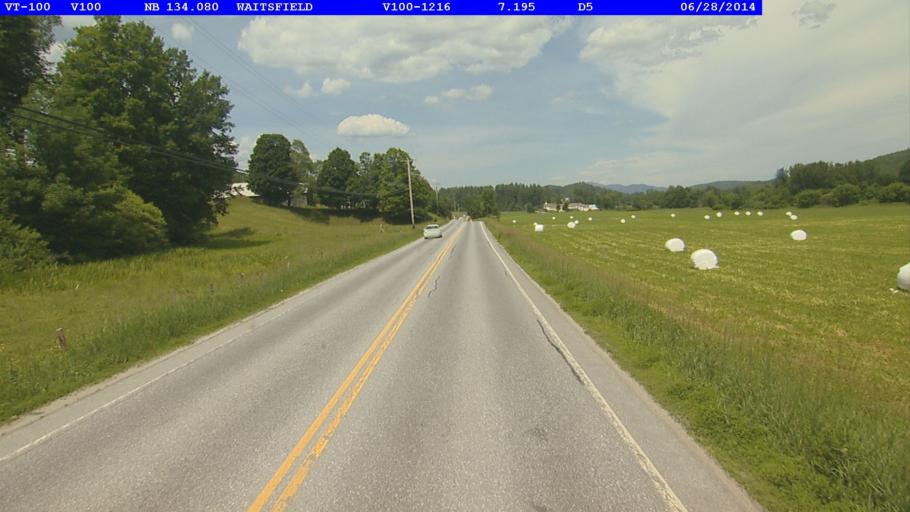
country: US
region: Vermont
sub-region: Washington County
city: Waterbury
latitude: 44.2301
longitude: -72.7833
